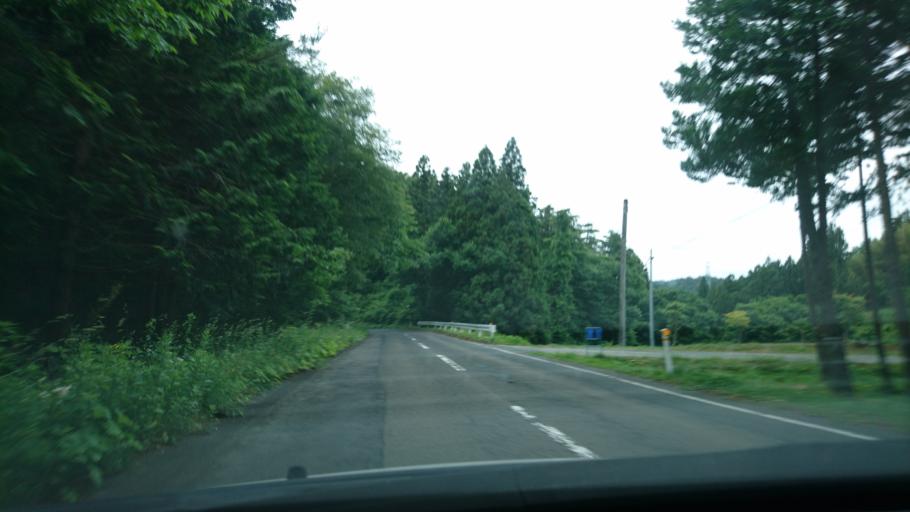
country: JP
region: Iwate
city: Ichinoseki
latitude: 38.9448
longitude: 141.2759
